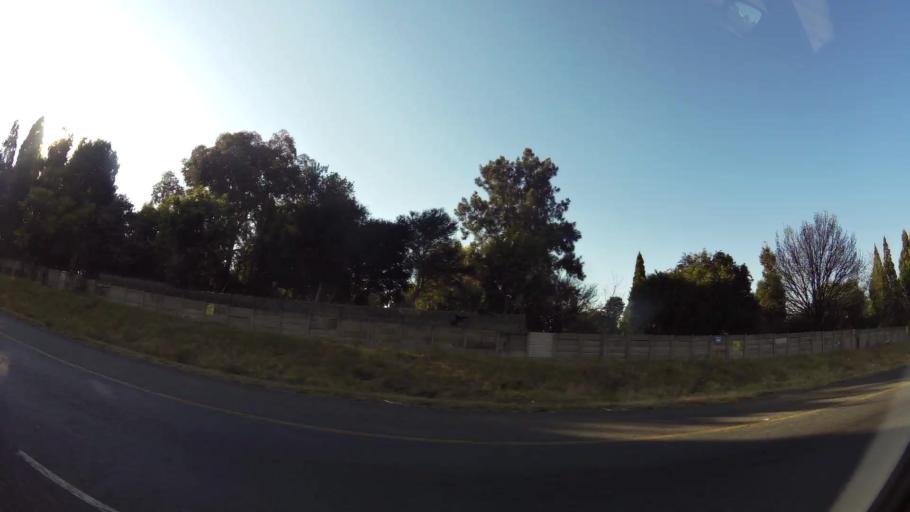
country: ZA
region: Gauteng
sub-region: Ekurhuleni Metropolitan Municipality
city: Germiston
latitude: -26.3283
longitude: 28.1121
